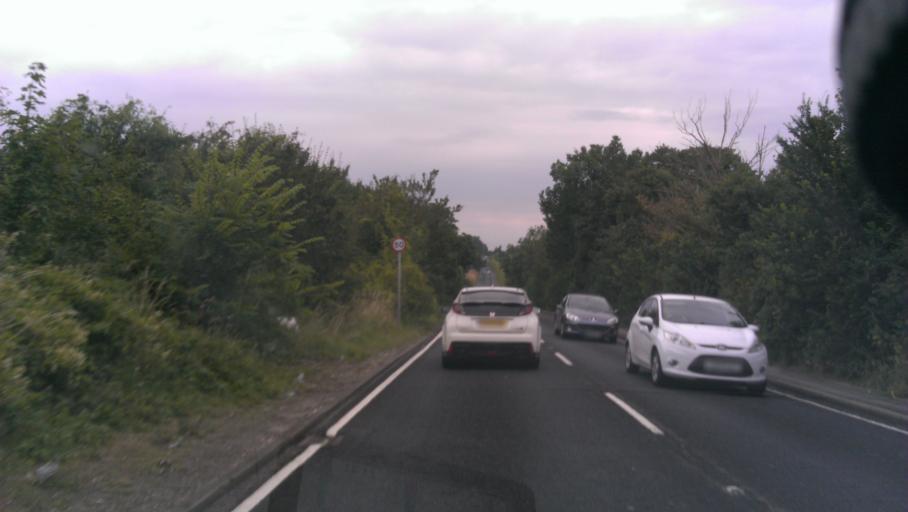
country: GB
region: England
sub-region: Kent
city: Faversham
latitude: 51.3025
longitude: 0.9209
